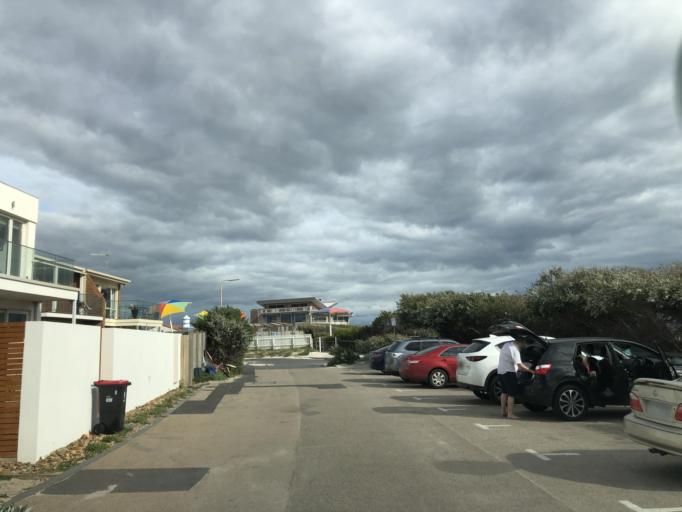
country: AU
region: Victoria
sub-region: Kingston
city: Bonbeach
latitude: -38.0753
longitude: 145.1209
